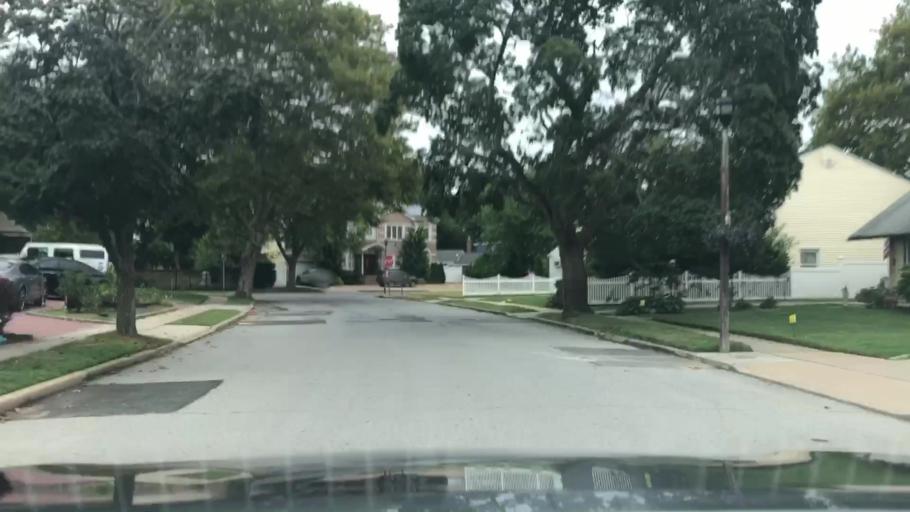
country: US
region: New York
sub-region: Nassau County
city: North Valley Stream
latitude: 40.6865
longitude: -73.6910
